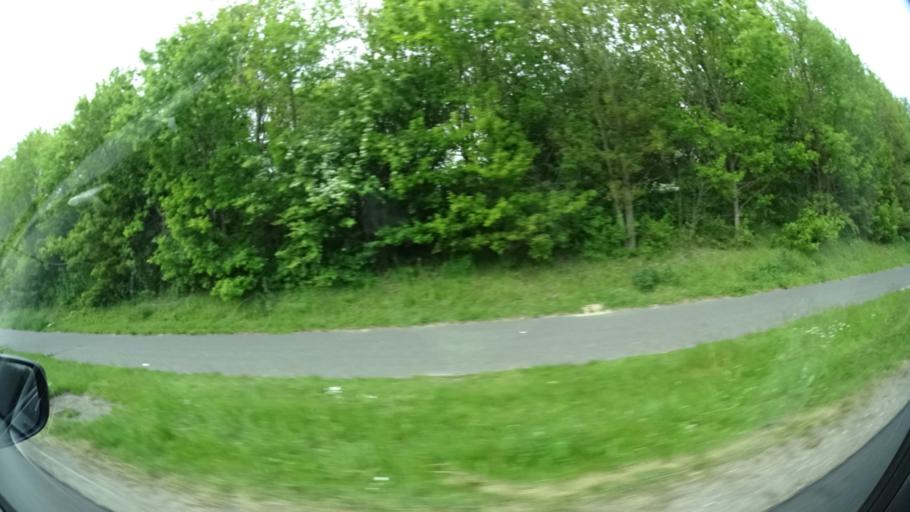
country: DK
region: Central Jutland
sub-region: Arhus Kommune
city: Marslet
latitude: 56.1088
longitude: 10.1842
